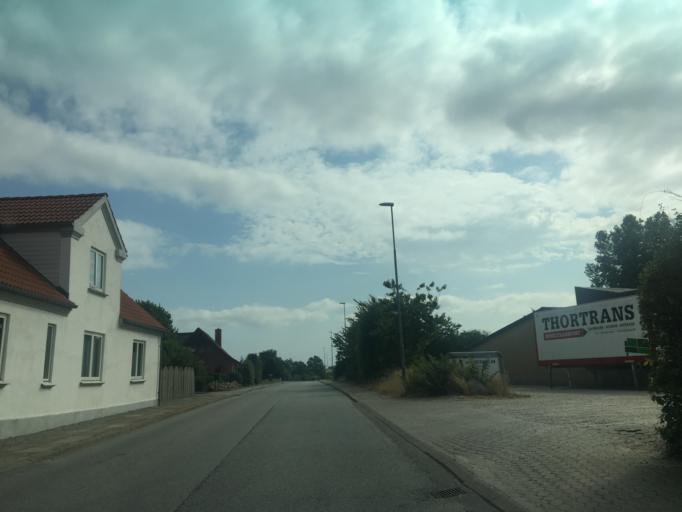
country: DK
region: North Denmark
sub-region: Thisted Kommune
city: Thisted
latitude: 56.8776
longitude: 8.6289
